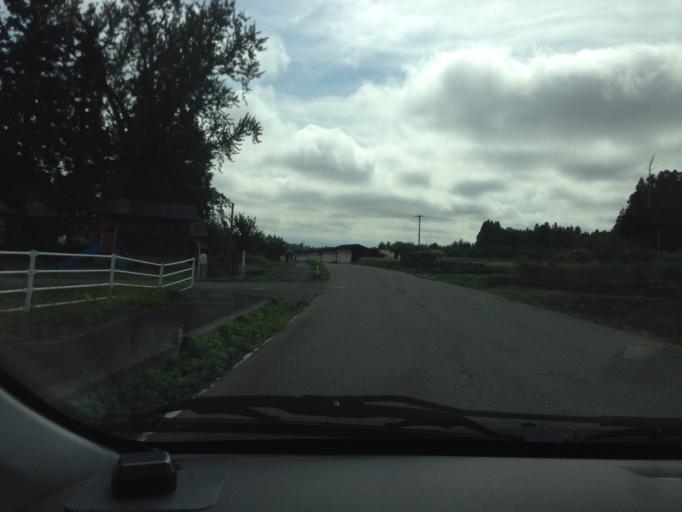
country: JP
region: Fukushima
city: Kitakata
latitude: 37.5266
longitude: 139.8026
